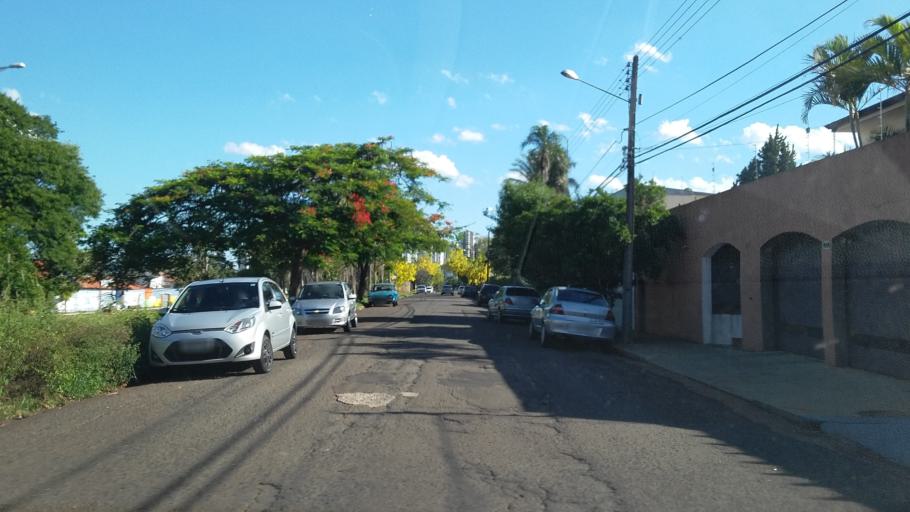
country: BR
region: Parana
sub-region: Londrina
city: Londrina
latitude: -23.3165
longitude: -51.1764
